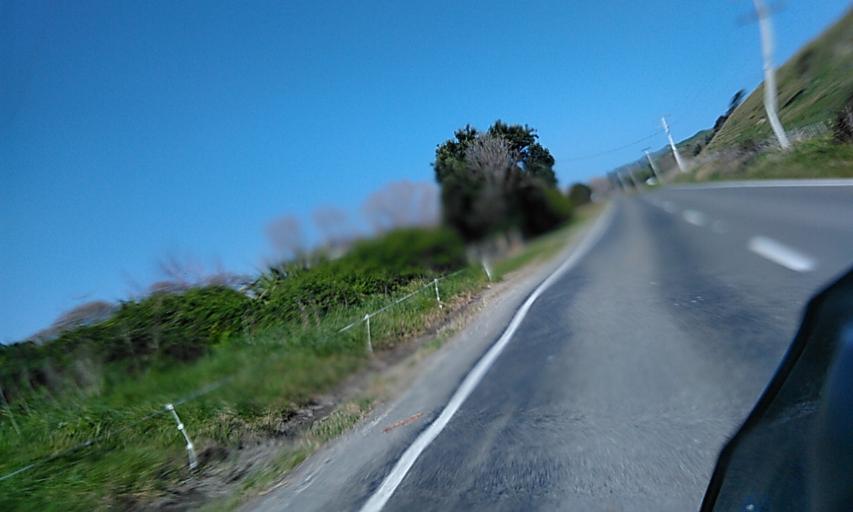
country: NZ
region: Gisborne
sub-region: Gisborne District
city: Gisborne
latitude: -38.3707
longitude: 178.2841
